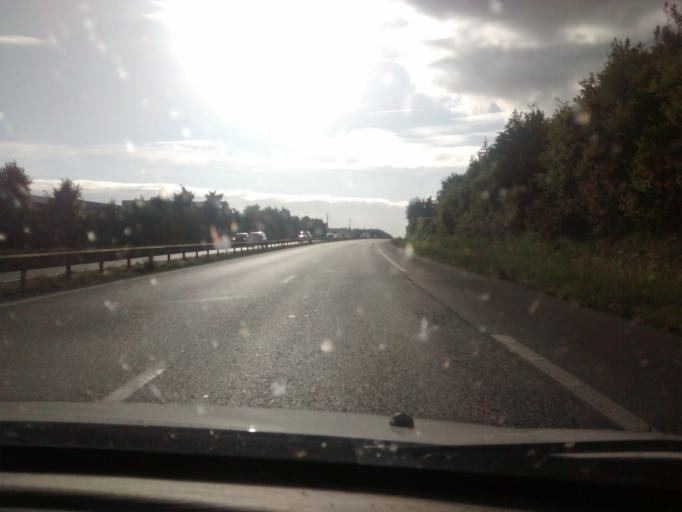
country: FR
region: Brittany
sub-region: Departement d'Ille-et-Vilaine
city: Noyal-sur-Vilaine
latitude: 48.1084
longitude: -1.5255
